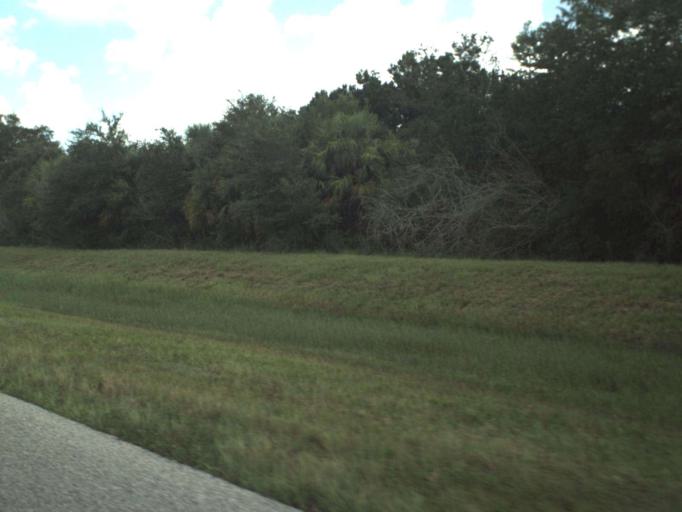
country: US
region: Florida
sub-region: Indian River County
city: West Vero Corridor
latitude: 27.6398
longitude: -80.5677
